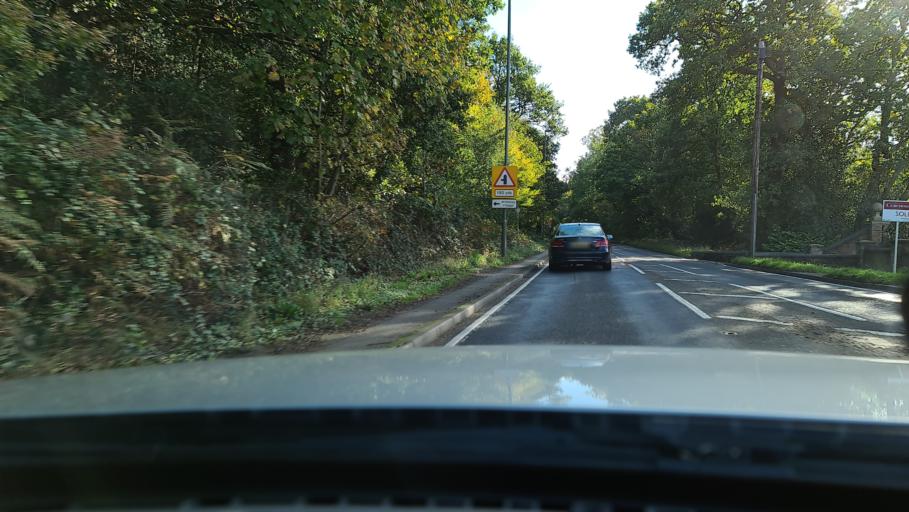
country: GB
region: England
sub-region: Surrey
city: Weybridge
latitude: 51.3528
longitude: -0.4344
